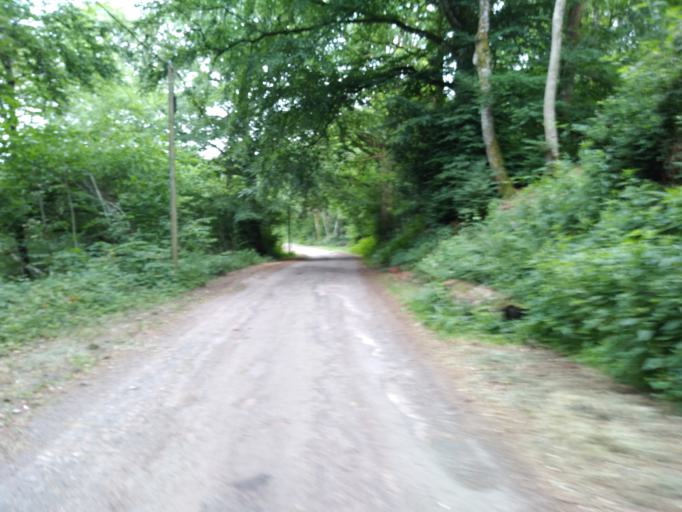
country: FR
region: Bourgogne
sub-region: Departement de la Cote-d'Or
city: Saulieu
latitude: 47.2753
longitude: 4.1259
